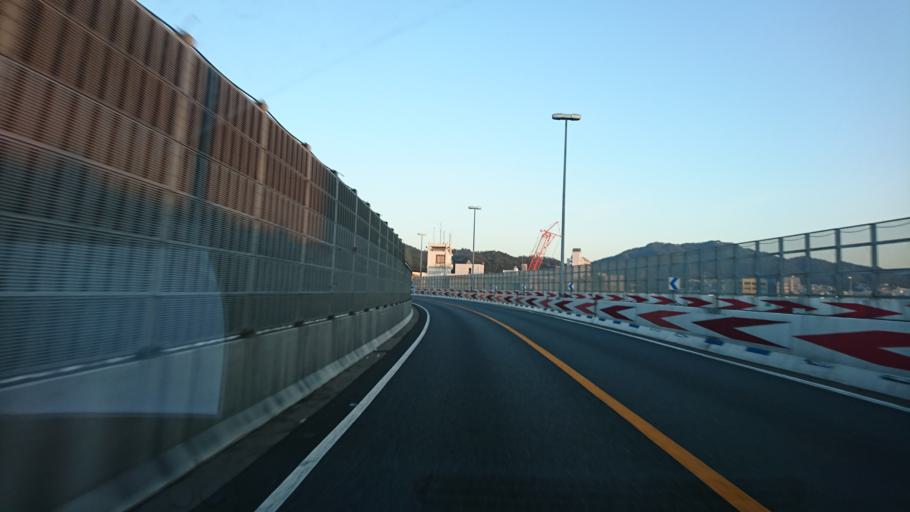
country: JP
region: Hyogo
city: Kobe
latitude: 34.6486
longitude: 135.1310
